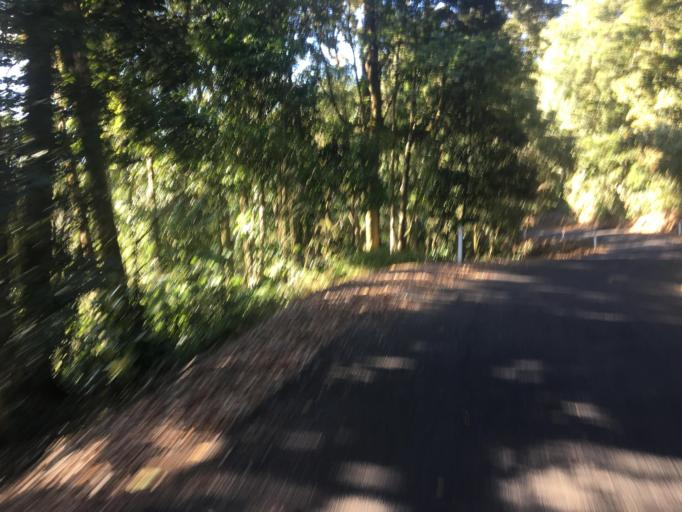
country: AU
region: Queensland
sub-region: Tablelands
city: Ravenshoe
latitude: -17.5890
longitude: 145.5915
